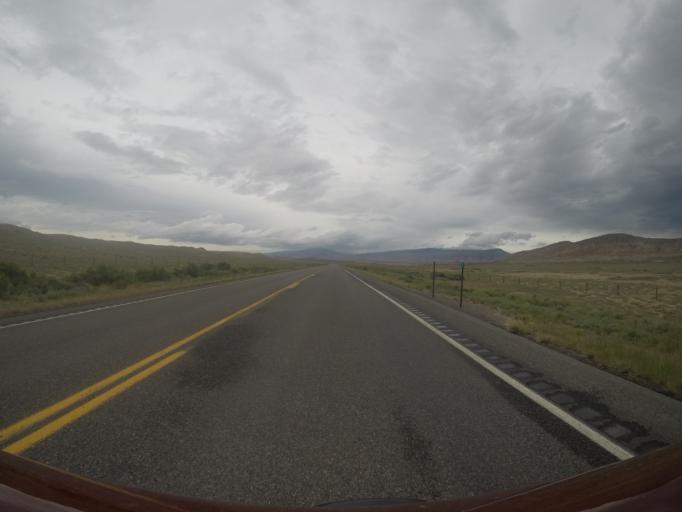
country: US
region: Wyoming
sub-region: Big Horn County
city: Lovell
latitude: 44.9182
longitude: -108.2946
